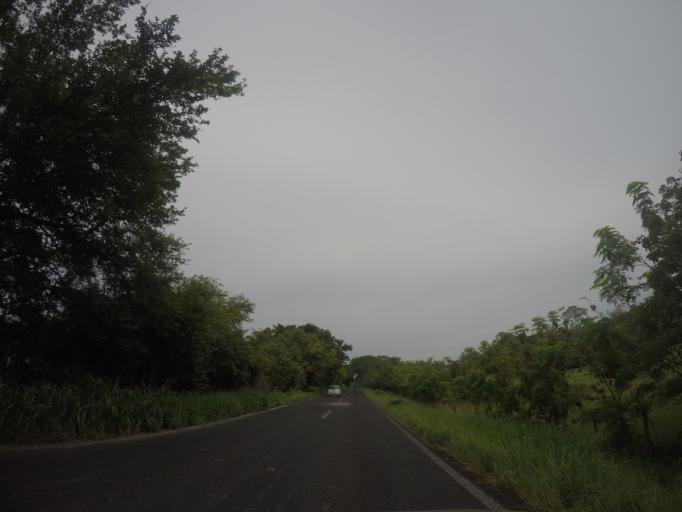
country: MX
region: Oaxaca
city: San Pedro Mixtepec
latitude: 15.9554
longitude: -97.2360
